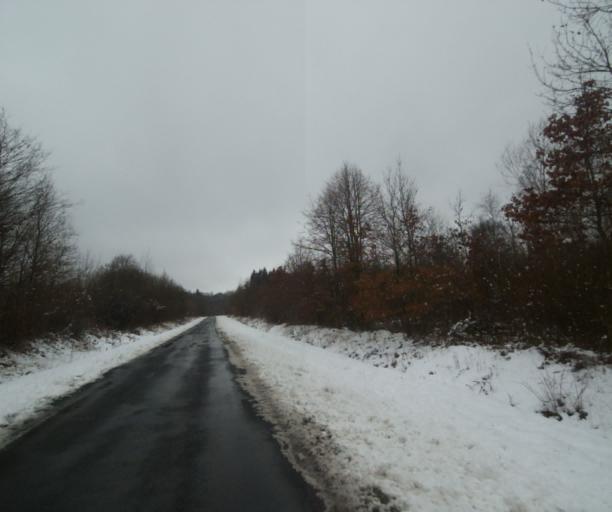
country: FR
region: Champagne-Ardenne
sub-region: Departement de la Haute-Marne
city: Laneuville-a-Remy
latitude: 48.4686
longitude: 4.8704
